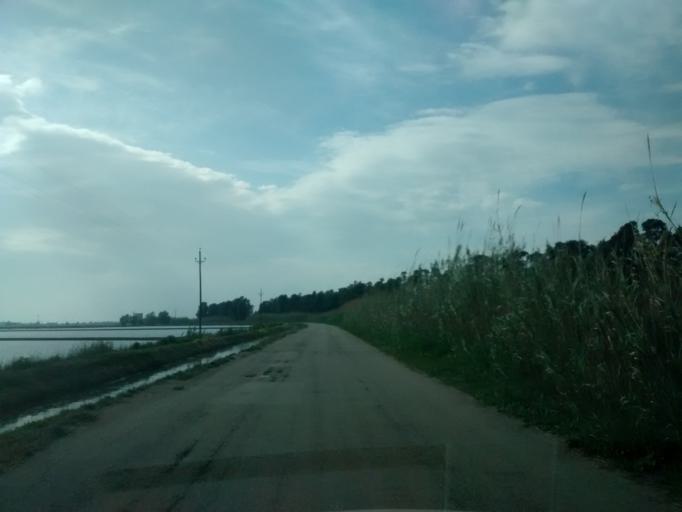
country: ES
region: Catalonia
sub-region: Provincia de Tarragona
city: Deltebre
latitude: 40.6973
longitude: 0.8348
